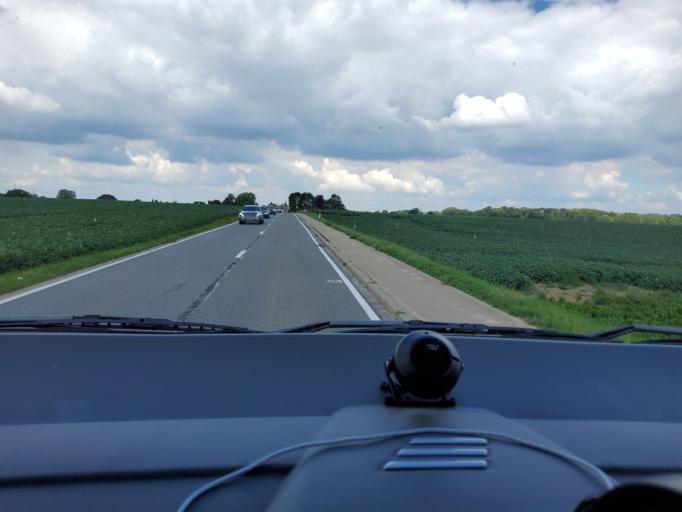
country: BE
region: Wallonia
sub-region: Province du Brabant Wallon
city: Genappe
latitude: 50.5787
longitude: 4.4272
